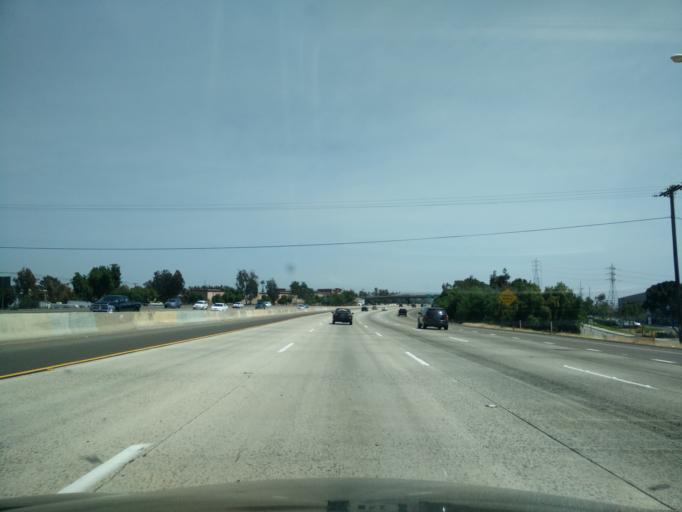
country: US
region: California
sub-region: San Diego County
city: Chula Vista
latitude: 32.6192
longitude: -117.0922
